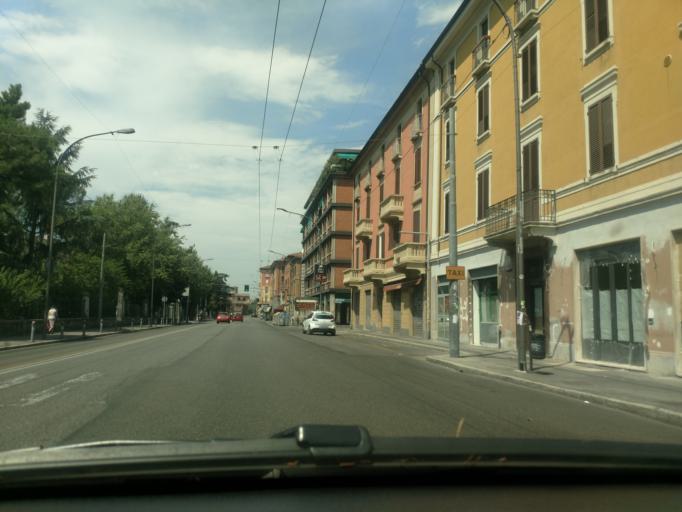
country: IT
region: Emilia-Romagna
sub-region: Provincia di Bologna
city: Bologna
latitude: 44.4925
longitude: 11.3630
